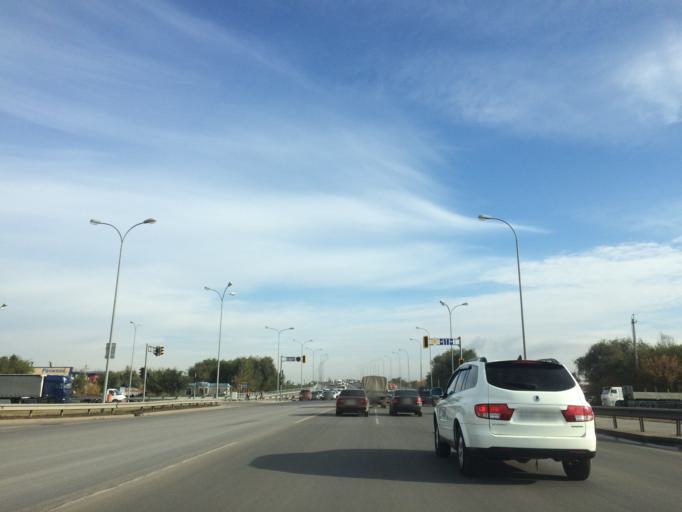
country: KZ
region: Astana Qalasy
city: Astana
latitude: 51.1680
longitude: 71.4778
